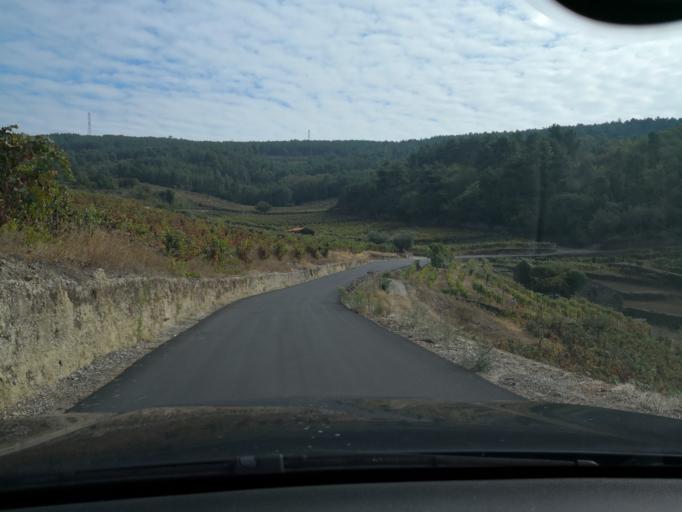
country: PT
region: Vila Real
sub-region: Sabrosa
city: Vilela
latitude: 41.2154
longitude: -7.6844
